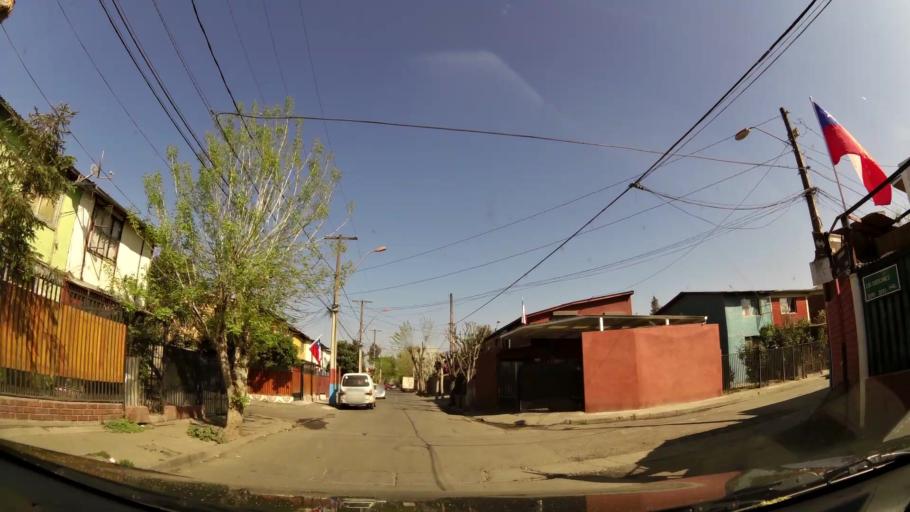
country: CL
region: Santiago Metropolitan
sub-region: Provincia de Chacabuco
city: Chicureo Abajo
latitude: -33.3560
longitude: -70.6878
